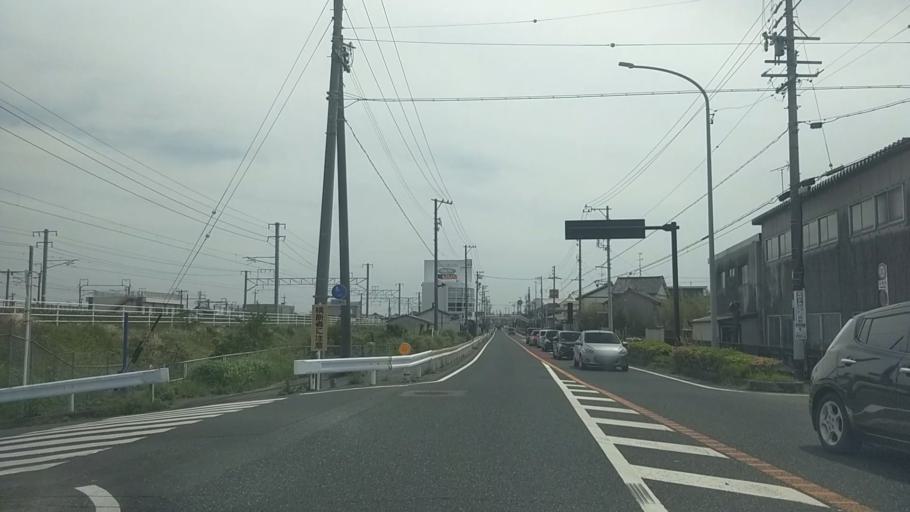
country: JP
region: Shizuoka
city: Kosai-shi
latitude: 34.6877
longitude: 137.6082
